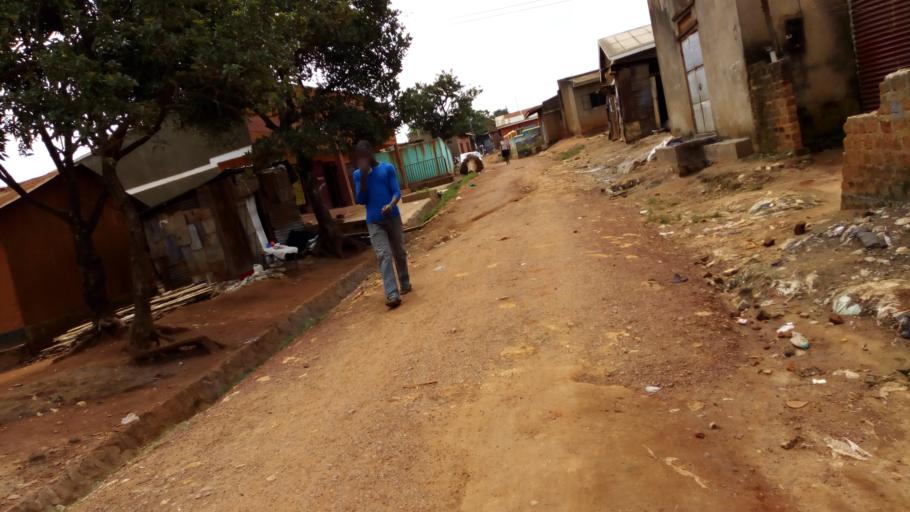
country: UG
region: Central Region
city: Kampala Central Division
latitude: 0.3779
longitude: 32.5613
